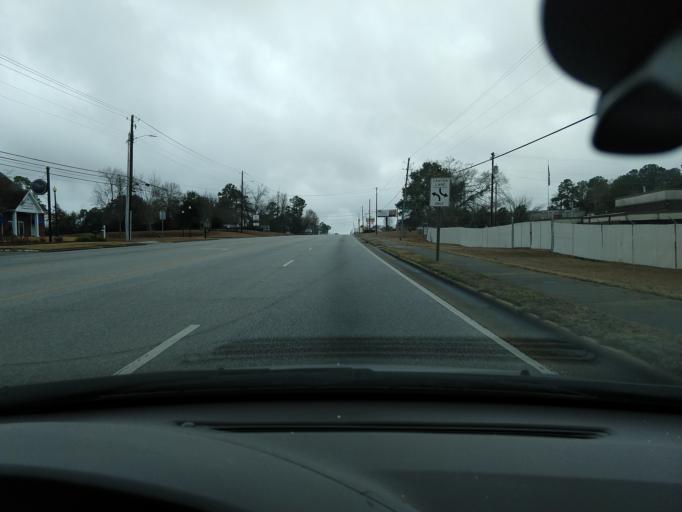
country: US
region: Alabama
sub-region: Houston County
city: Dothan
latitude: 31.2382
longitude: -85.4347
